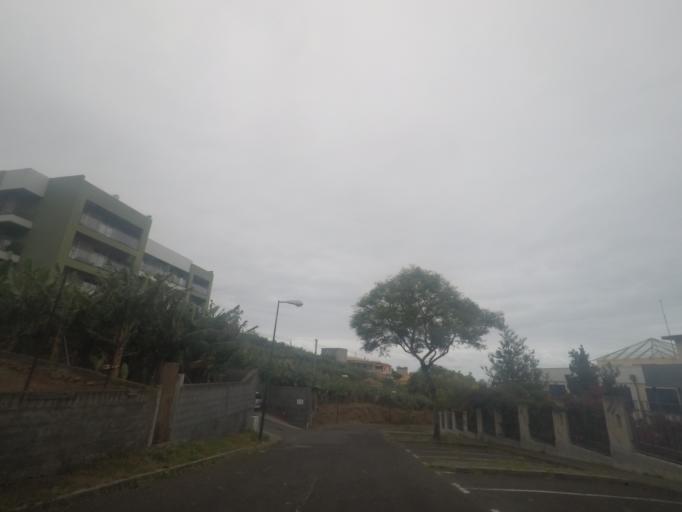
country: PT
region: Madeira
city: Camara de Lobos
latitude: 32.6541
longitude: -16.9815
